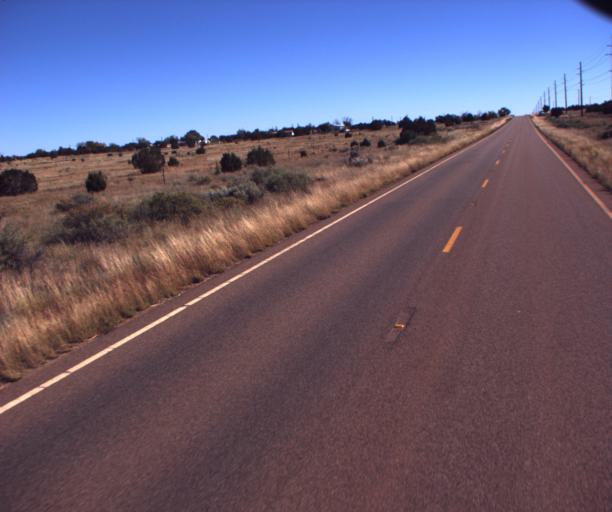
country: US
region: Arizona
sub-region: Navajo County
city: Taylor
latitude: 34.4841
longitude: -110.2585
